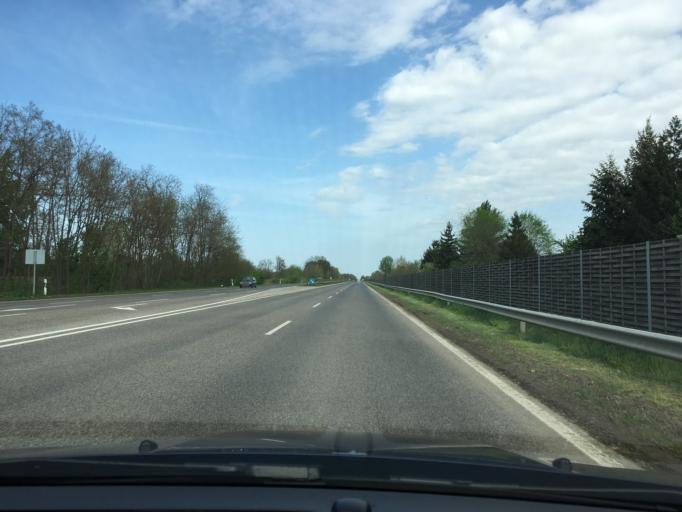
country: HU
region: Csongrad
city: Hodmezovasarhely
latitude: 46.3909
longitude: 20.2801
